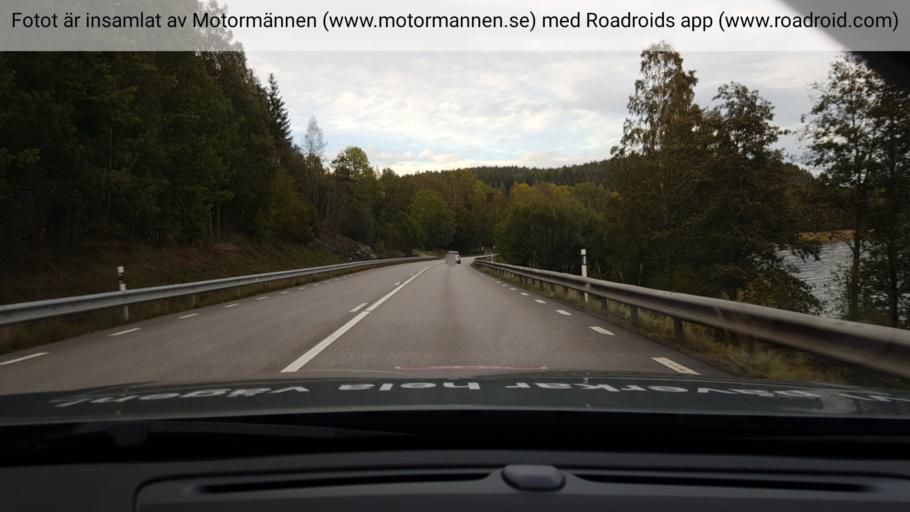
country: SE
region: Vaestra Goetaland
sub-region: Bengtsfors Kommun
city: Bengtsfors
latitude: 59.0348
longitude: 12.3139
